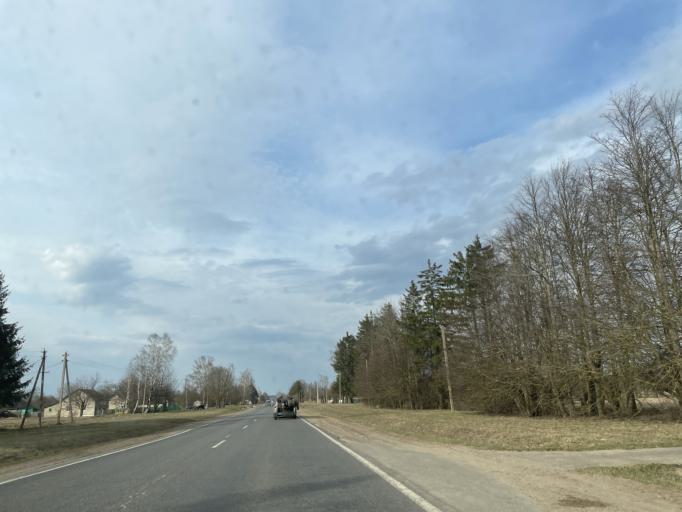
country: BY
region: Minsk
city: Klyetsk
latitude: 53.1201
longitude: 26.6653
